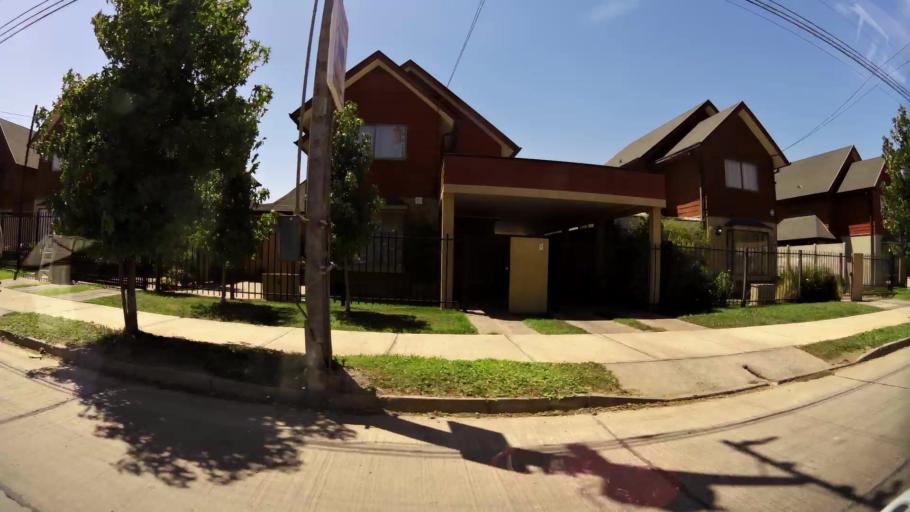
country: CL
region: Maule
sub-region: Provincia de Talca
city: Talca
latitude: -35.4297
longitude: -71.6194
